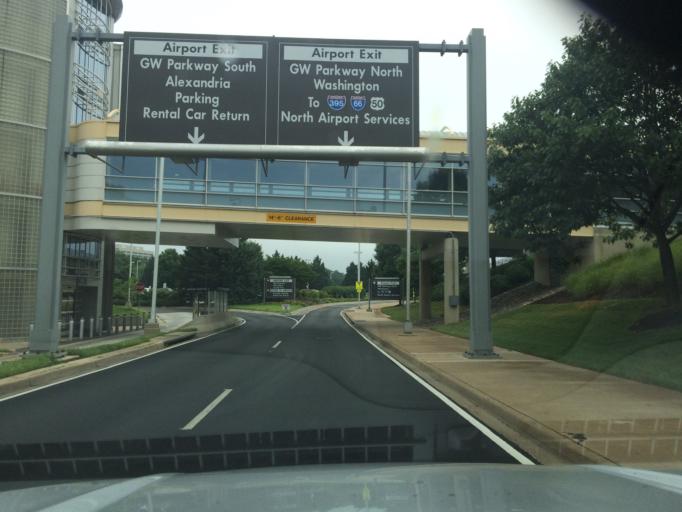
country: US
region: Washington, D.C.
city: Washington, D.C.
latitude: 38.8543
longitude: -77.0448
